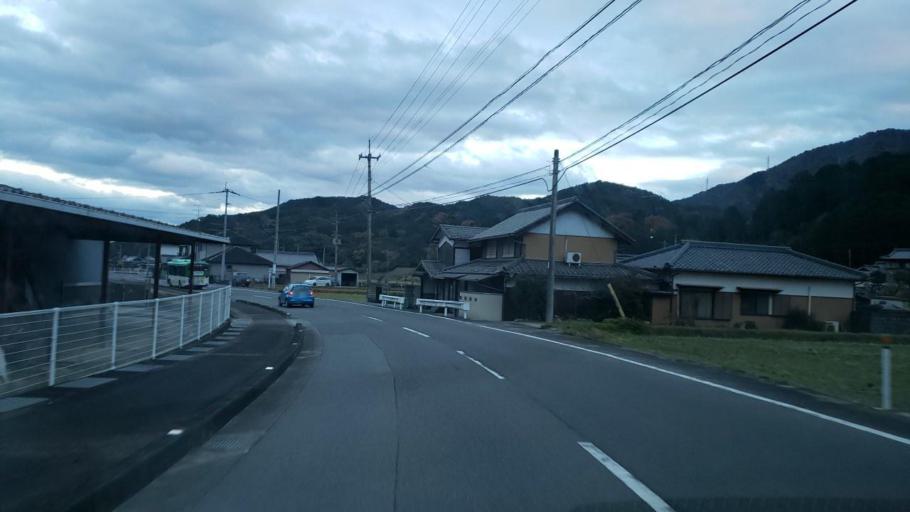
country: JP
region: Tokushima
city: Kamojimacho-jogejima
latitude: 34.2024
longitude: 134.3074
